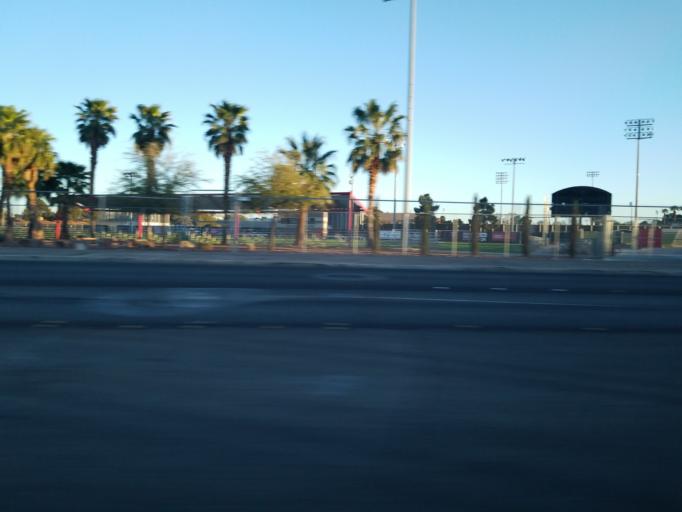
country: US
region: Nevada
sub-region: Clark County
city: Paradise
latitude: 36.1132
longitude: -115.1475
